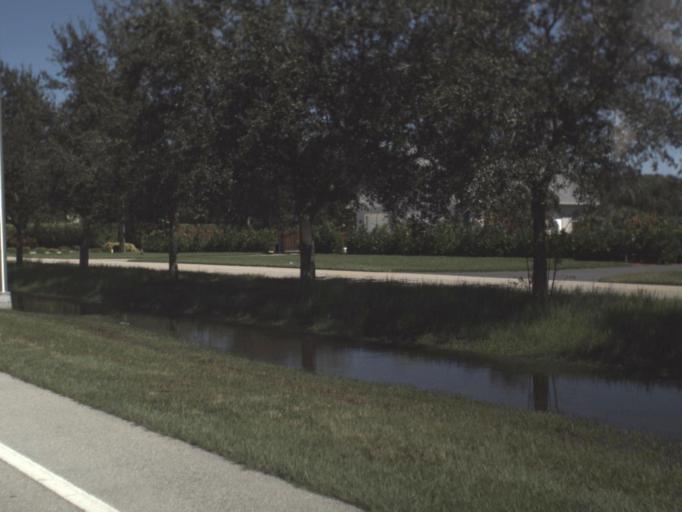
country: US
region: Florida
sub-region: Collier County
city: Pine Ridge
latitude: 26.2274
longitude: -81.8006
